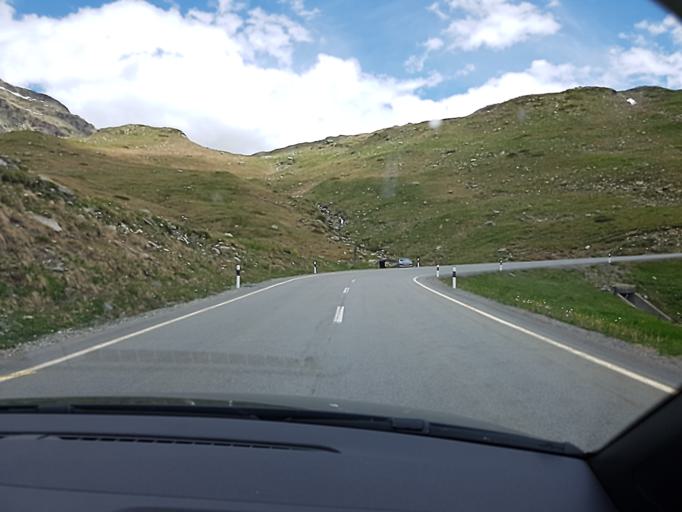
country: CH
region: Grisons
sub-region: Bernina District
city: Poschiavo
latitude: 46.4166
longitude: 10.0200
